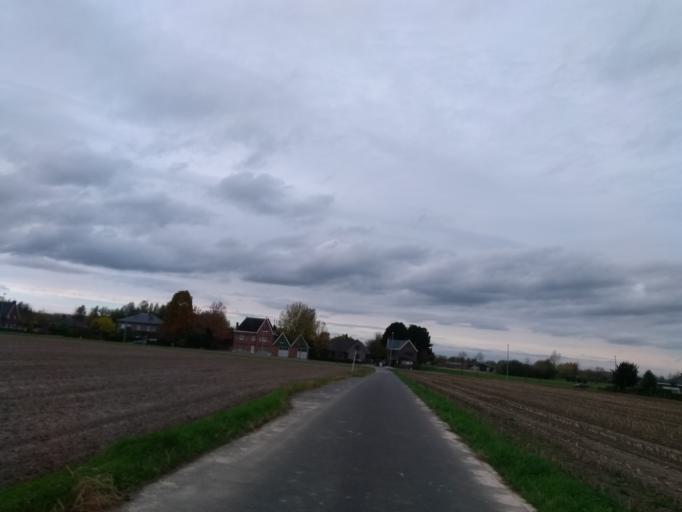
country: BE
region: Flanders
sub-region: Provincie Oost-Vlaanderen
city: Oosterzele
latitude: 50.9259
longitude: 3.7668
